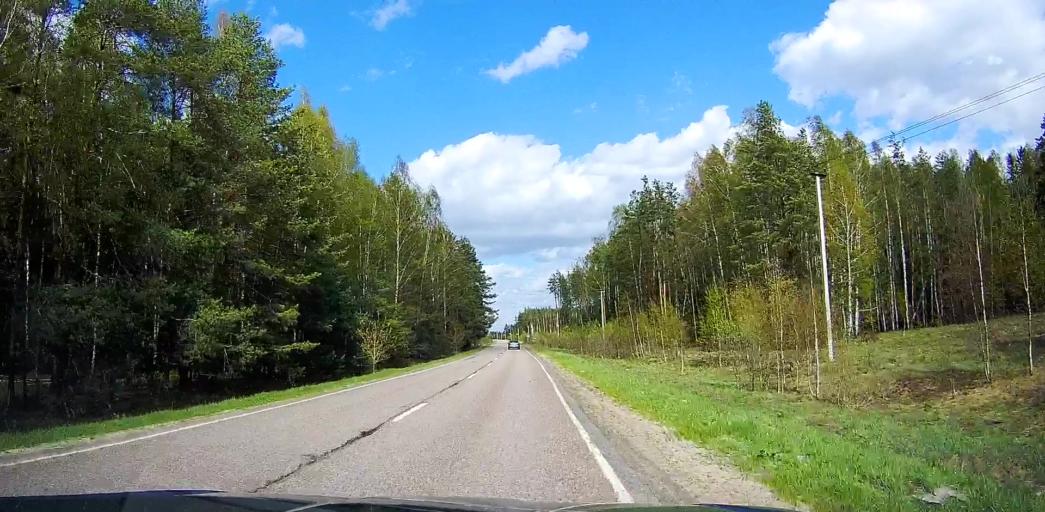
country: RU
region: Moskovskaya
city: Davydovo
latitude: 55.5920
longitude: 38.8340
